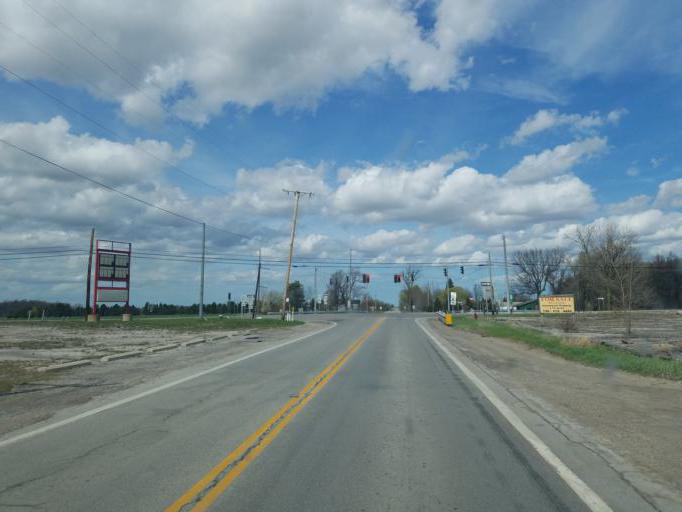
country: US
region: Ohio
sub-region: Huron County
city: Bellevue
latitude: 41.2645
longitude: -82.7951
